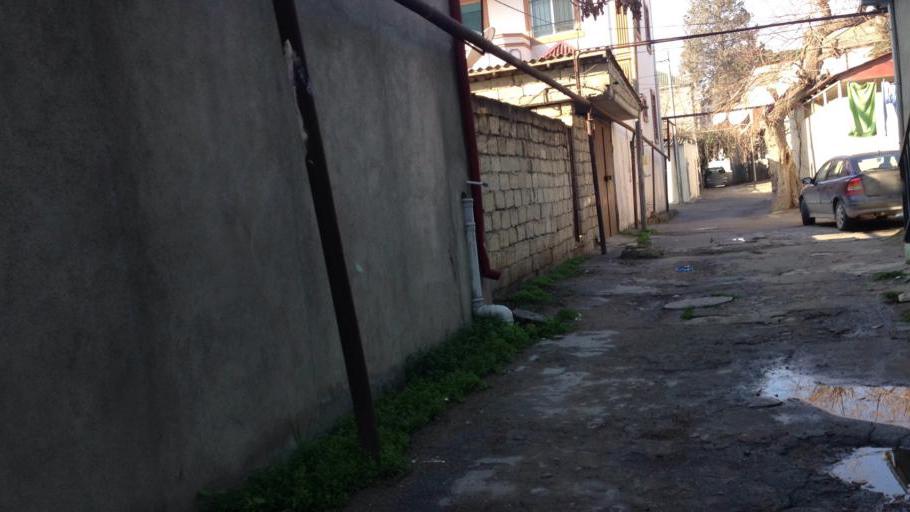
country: AZ
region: Baki
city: Binagadi
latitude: 40.4374
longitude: 49.8495
